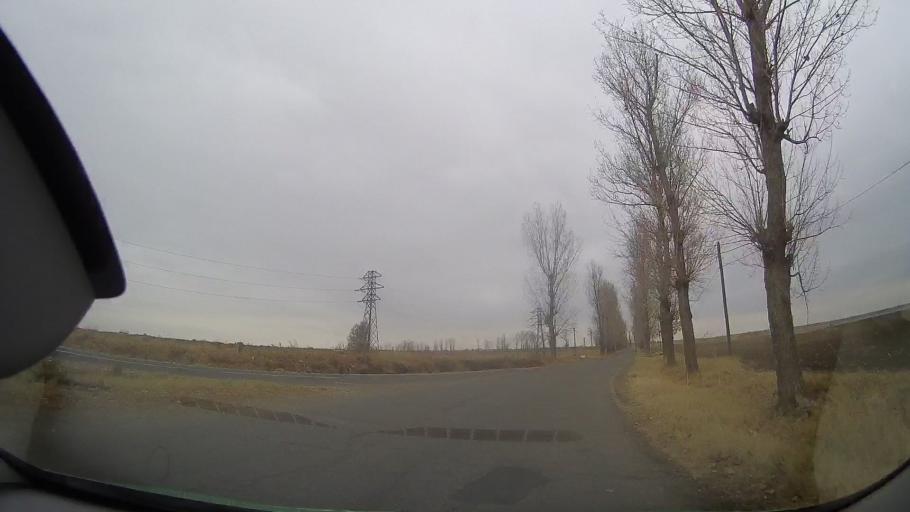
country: RO
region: Buzau
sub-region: Comuna Rusetu
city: Rusetu
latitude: 44.9443
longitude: 27.2311
